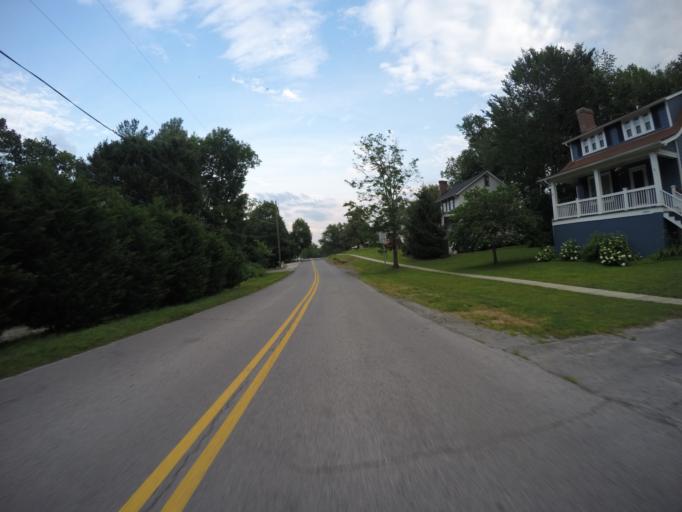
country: US
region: Tennessee
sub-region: Davidson County
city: Lakewood
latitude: 36.2561
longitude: -86.6423
